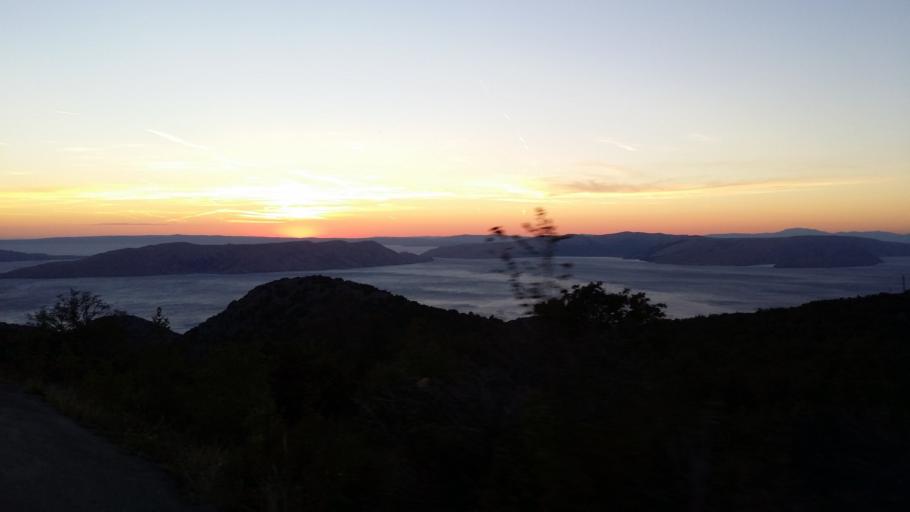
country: HR
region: Licko-Senjska
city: Senj
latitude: 44.9081
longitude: 14.9484
